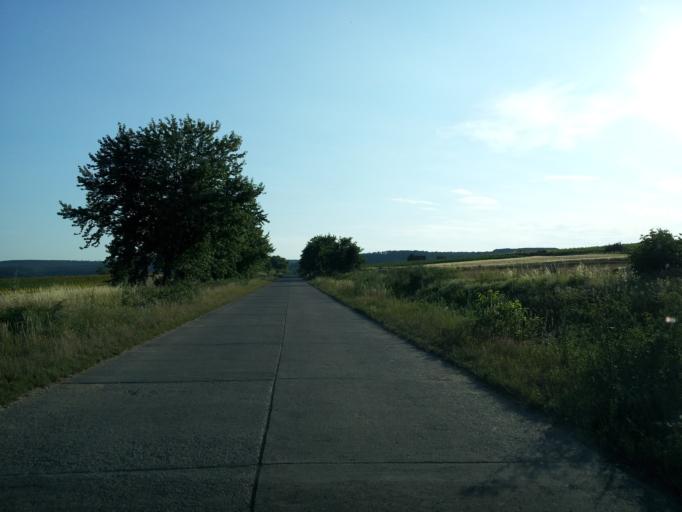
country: HU
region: Veszprem
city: Urkut
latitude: 46.9811
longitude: 17.5864
